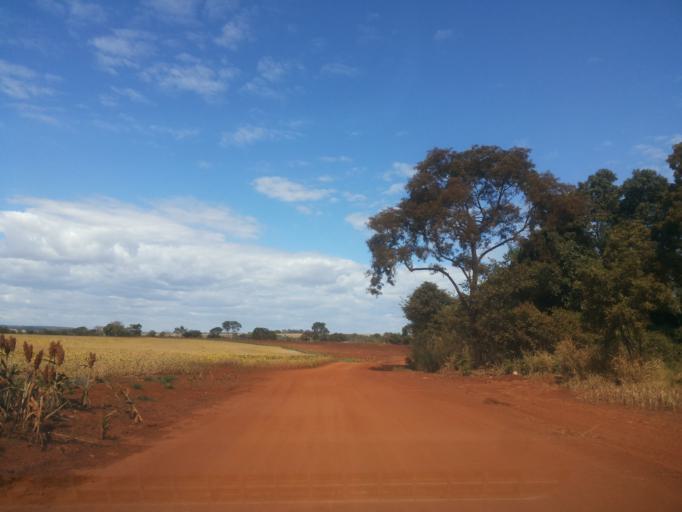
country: BR
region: Minas Gerais
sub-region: Centralina
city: Centralina
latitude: -18.5665
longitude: -49.2257
